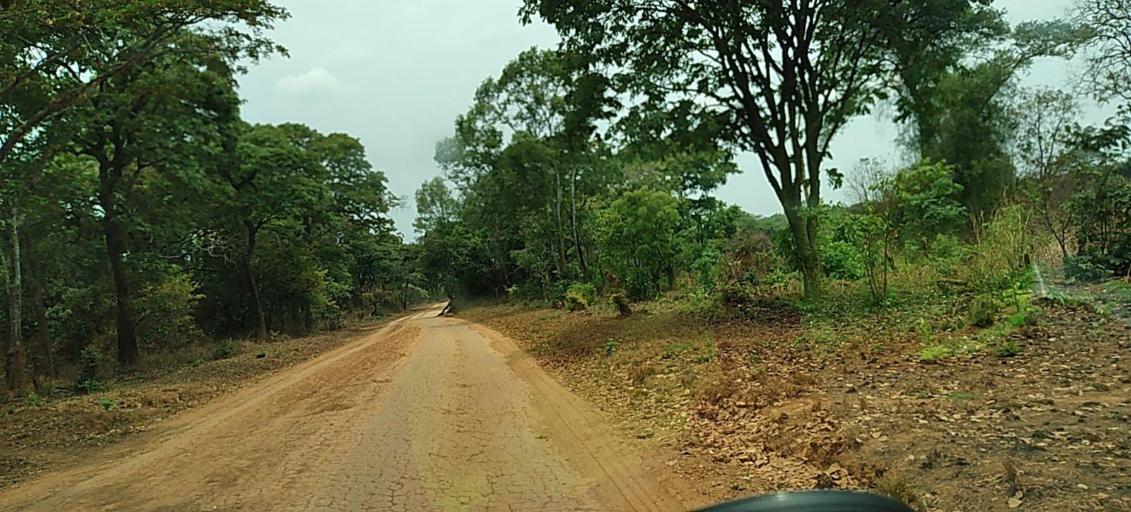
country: ZM
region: North-Western
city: Solwezi
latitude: -12.8204
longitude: 26.5366
